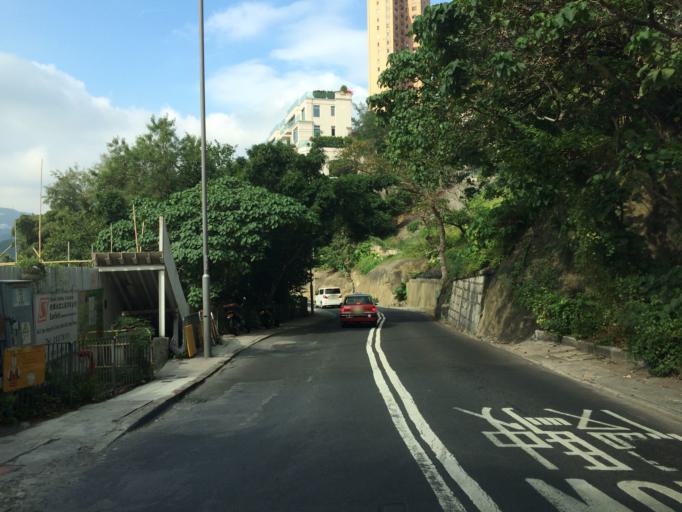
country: HK
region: Wanchai
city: Wan Chai
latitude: 22.2378
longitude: 114.1894
